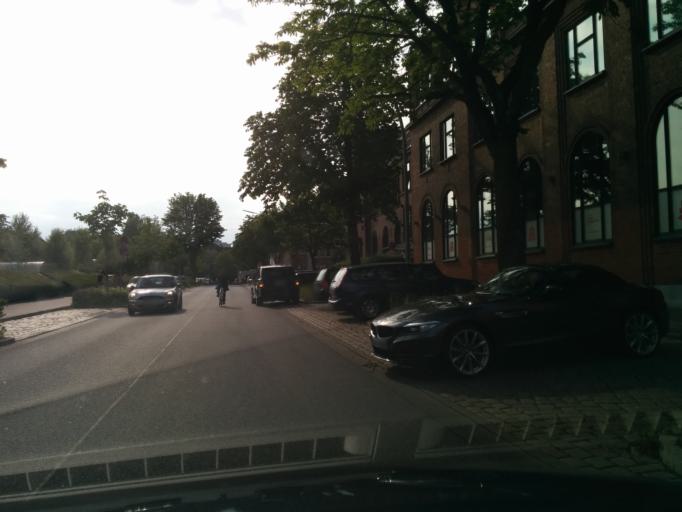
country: DE
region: Hamburg
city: Altona
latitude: 53.5609
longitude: 9.9144
